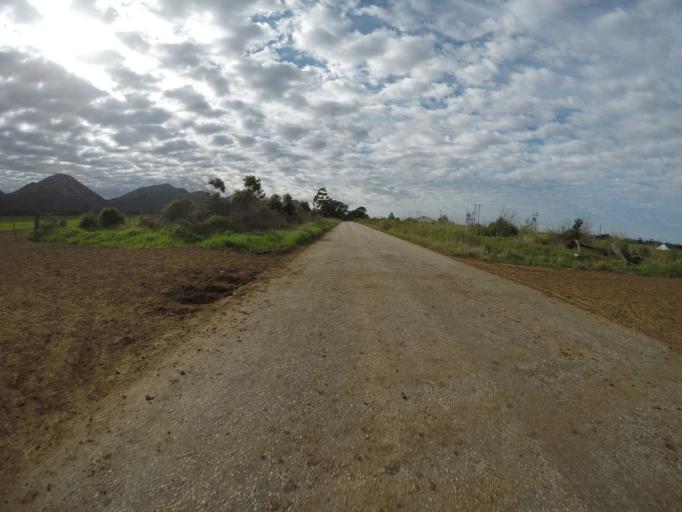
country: ZA
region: Eastern Cape
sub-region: Cacadu District Municipality
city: Kareedouw
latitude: -34.0452
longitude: 24.4446
